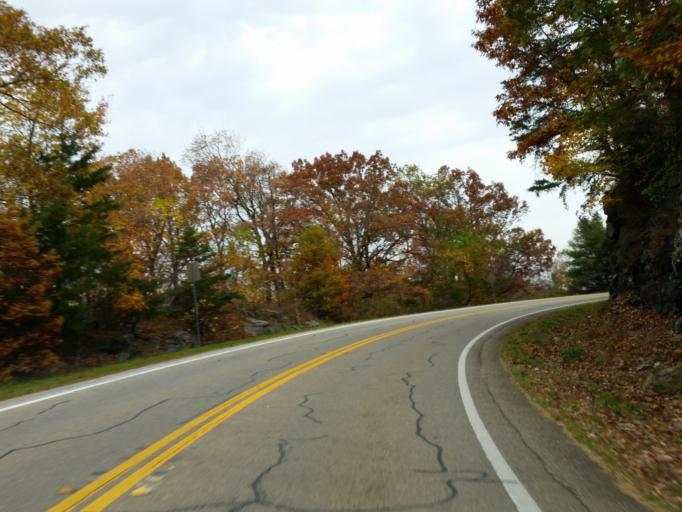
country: US
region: Georgia
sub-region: Pickens County
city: Jasper
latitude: 34.5433
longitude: -84.3706
